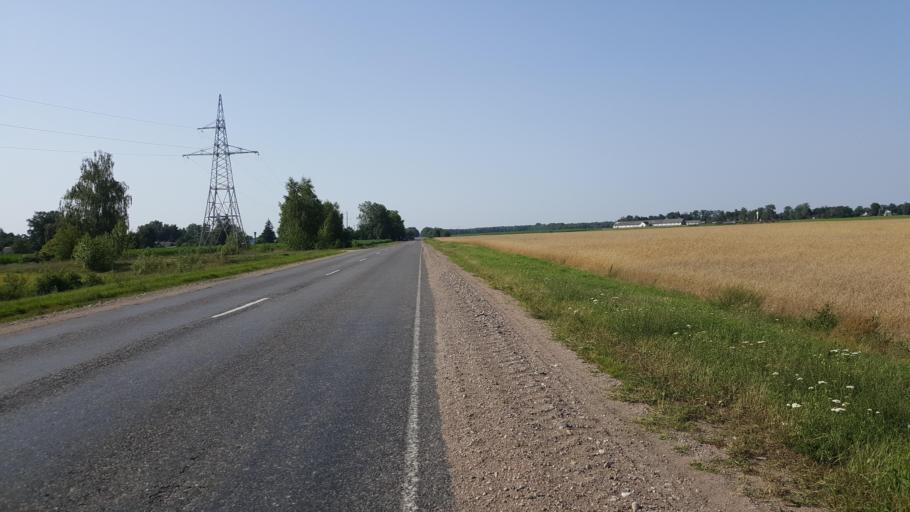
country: BY
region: Brest
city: Zhabinka
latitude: 52.2518
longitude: 23.9690
